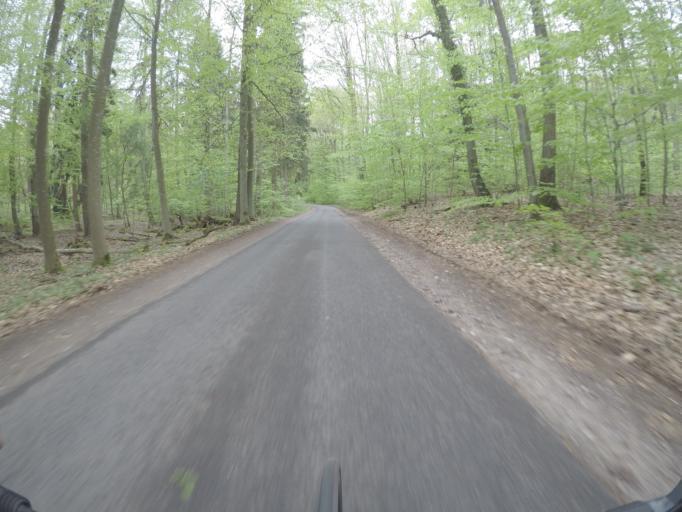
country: DE
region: Brandenburg
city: Marienwerder
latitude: 52.8962
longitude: 13.6524
